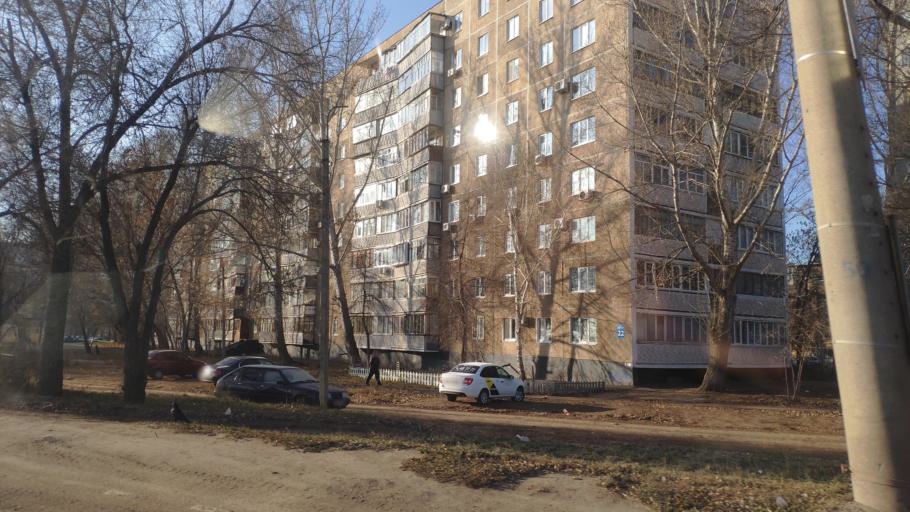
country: RU
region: Orenburg
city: Prigorodnyy
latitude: 51.7782
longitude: 55.1905
